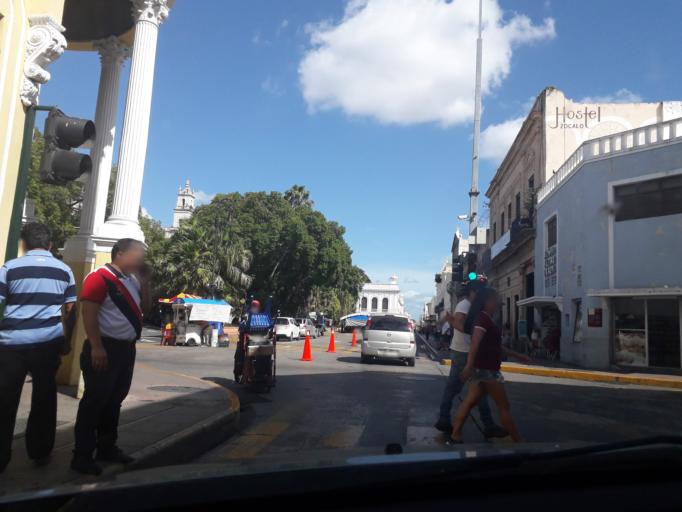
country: MX
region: Yucatan
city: Merida
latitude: 20.9667
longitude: -89.6247
